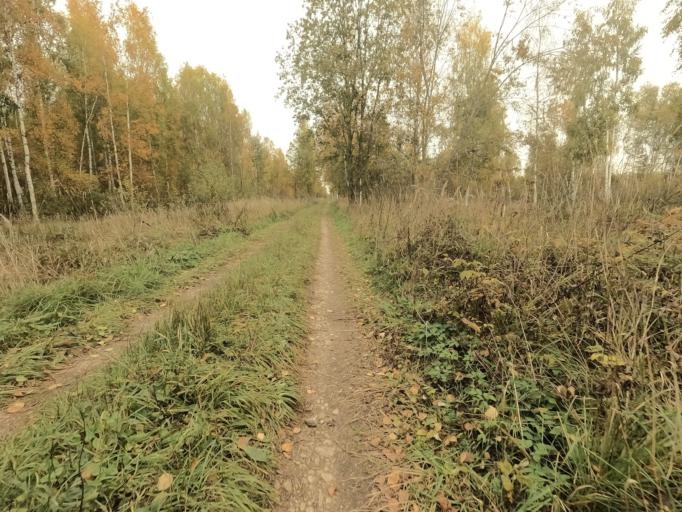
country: RU
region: Novgorod
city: Pankovka
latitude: 58.8774
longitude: 30.9411
